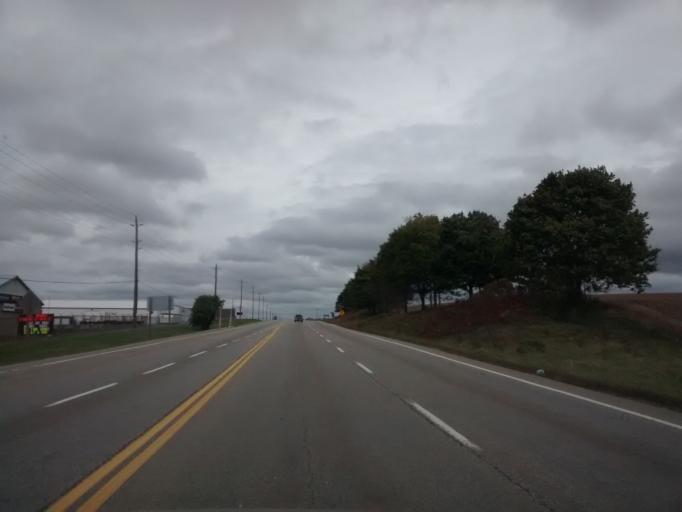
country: CA
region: Ontario
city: Ancaster
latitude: 43.0903
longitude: -79.9477
